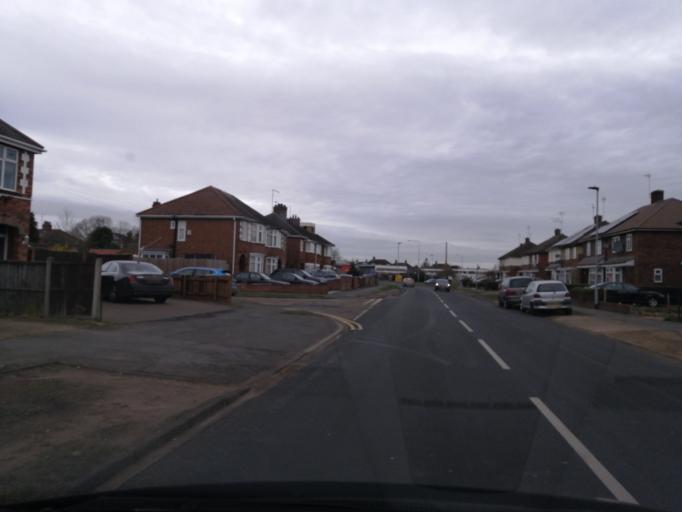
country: GB
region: England
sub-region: Peterborough
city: Peterborough
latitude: 52.5948
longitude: -0.2390
